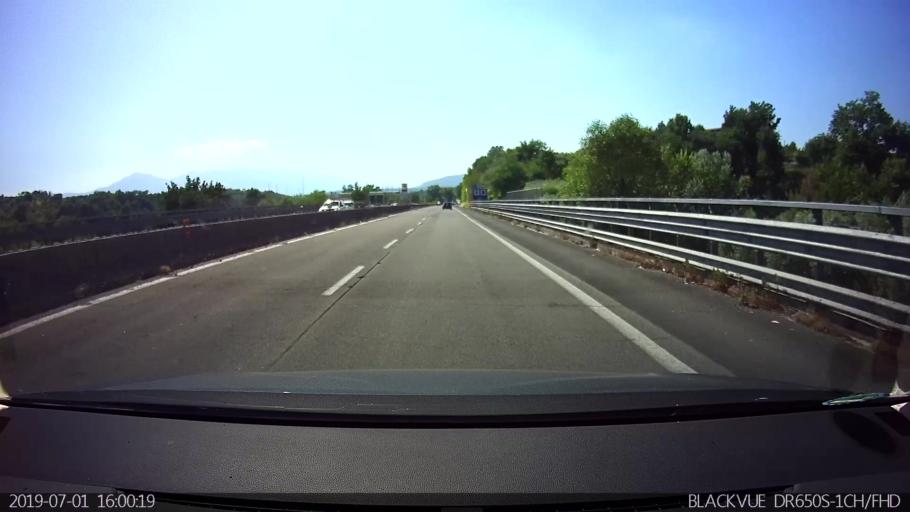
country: IT
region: Latium
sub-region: Provincia di Frosinone
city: San Giuseppe le Prata-Cotropagno
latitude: 41.6625
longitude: 13.3998
